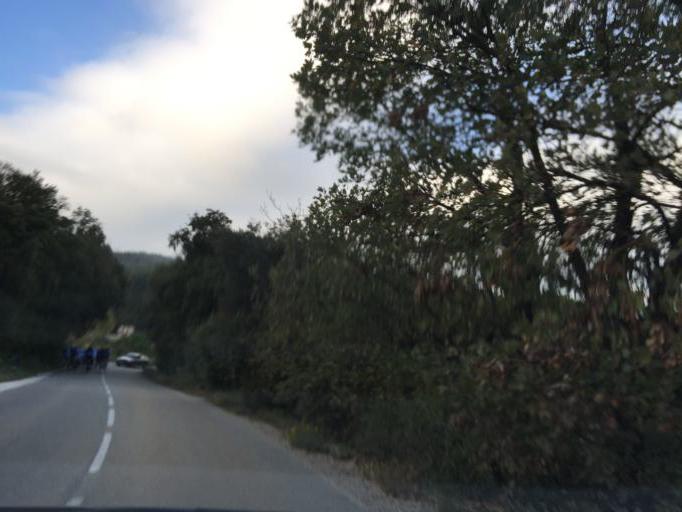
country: FR
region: Rhone-Alpes
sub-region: Departement de la Drome
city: Malataverne
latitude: 44.4860
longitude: 4.7433
